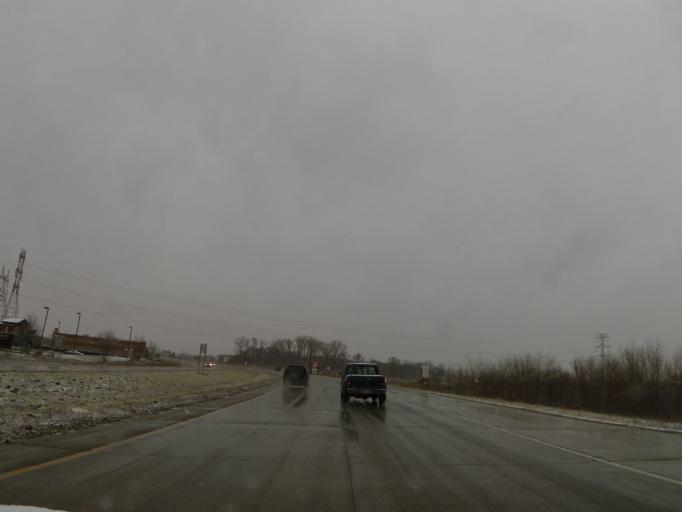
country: US
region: Minnesota
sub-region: Scott County
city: Prior Lake
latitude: 44.7752
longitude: -93.4136
